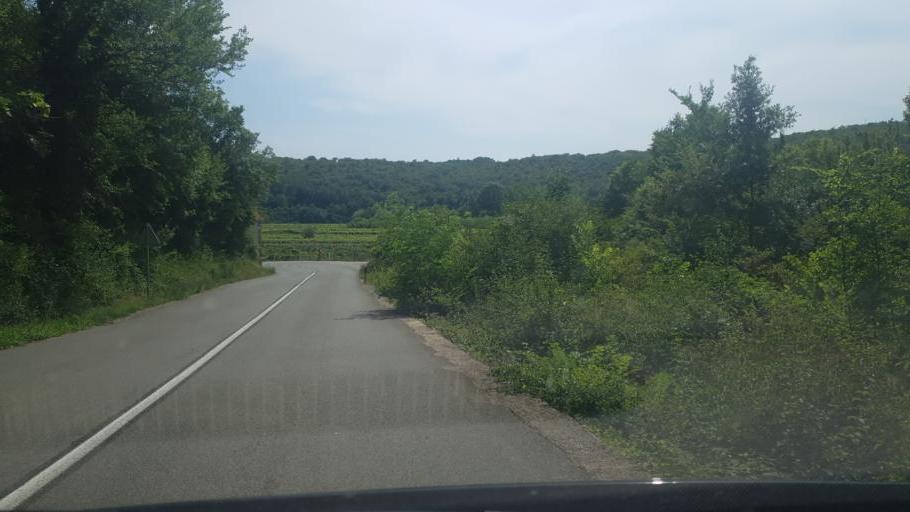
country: HR
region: Primorsko-Goranska
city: Punat
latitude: 45.0900
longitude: 14.6421
